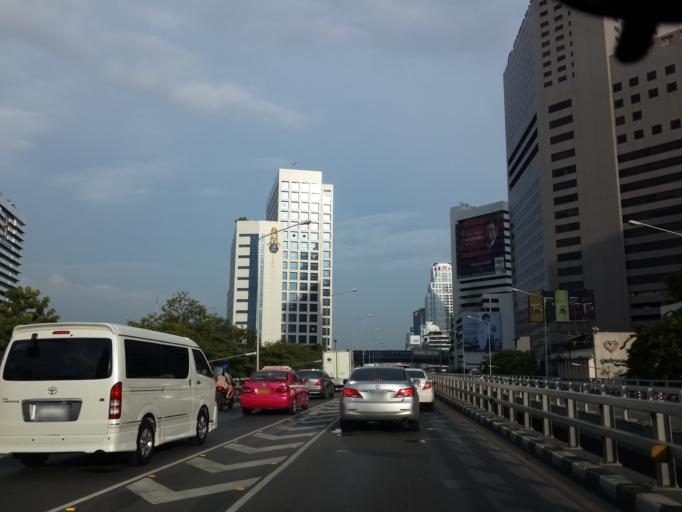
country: TH
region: Bangkok
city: Bang Rak
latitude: 13.7308
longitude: 100.5336
